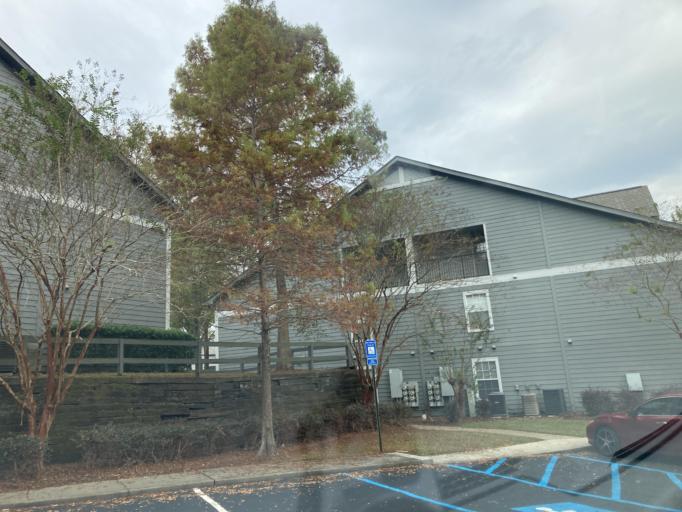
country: US
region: Mississippi
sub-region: Lamar County
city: West Hattiesburg
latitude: 31.3020
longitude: -89.3739
